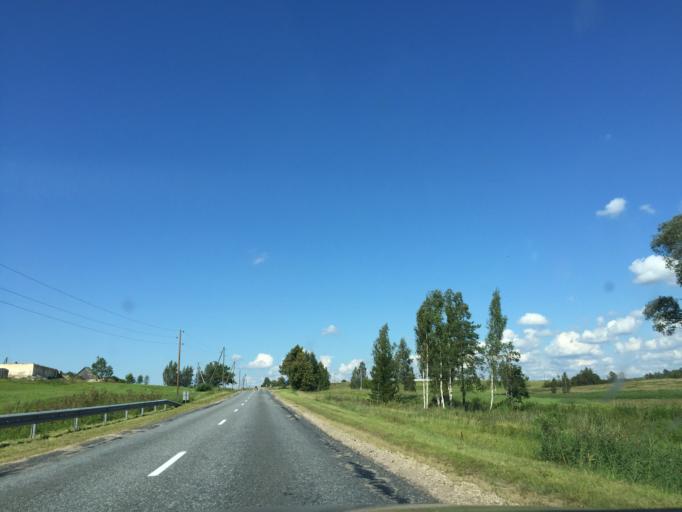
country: LV
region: Limbazu Rajons
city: Limbazi
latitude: 57.4454
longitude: 24.7242
